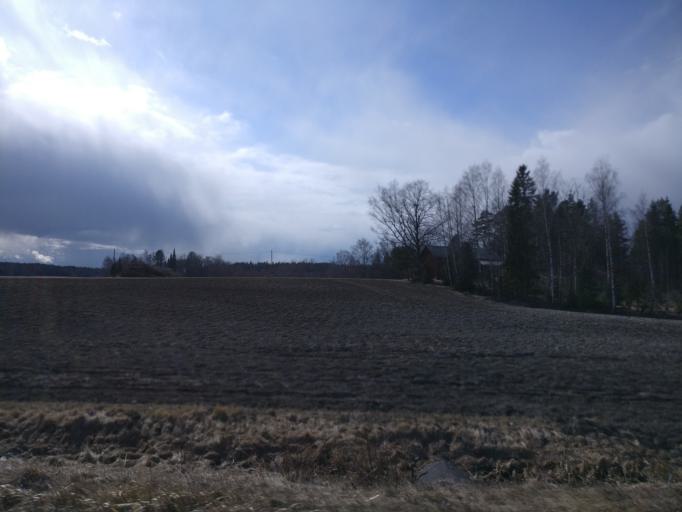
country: FI
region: Uusimaa
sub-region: Raaseporin
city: Inga
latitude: 60.1141
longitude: 23.8819
